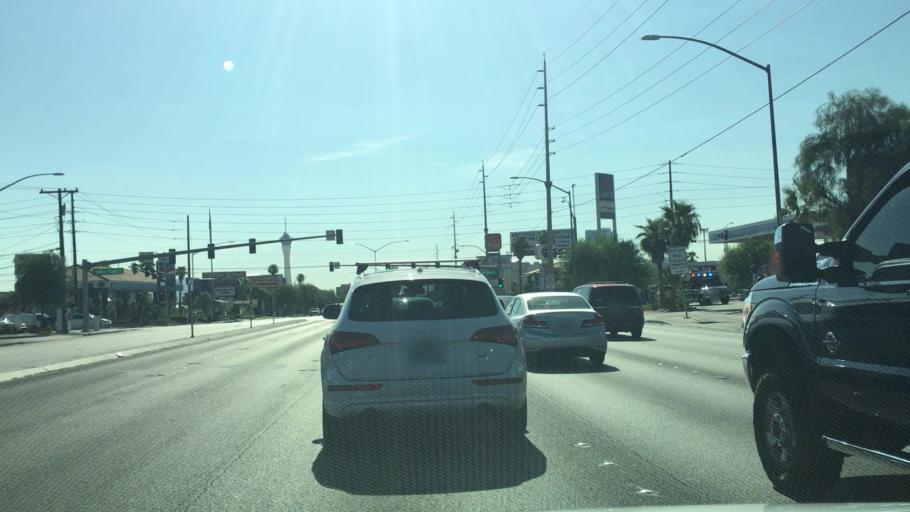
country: US
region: Nevada
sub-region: Clark County
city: Las Vegas
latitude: 36.1444
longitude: -115.1919
